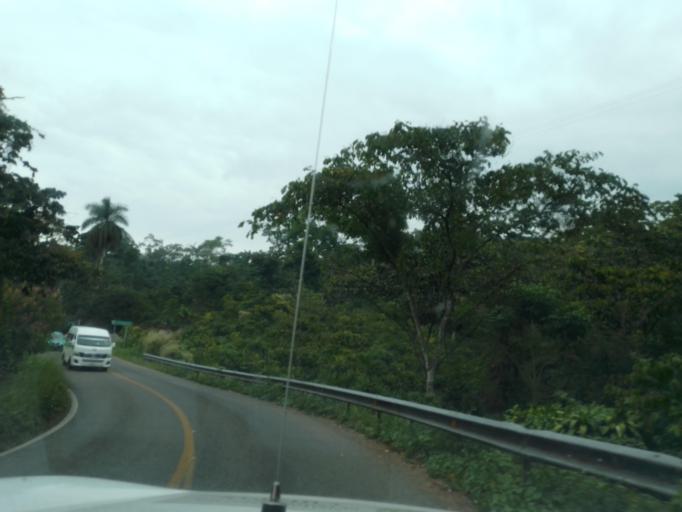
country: MX
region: Chiapas
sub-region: Union Juarez
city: Santo Domingo
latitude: 15.0378
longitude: -92.1215
